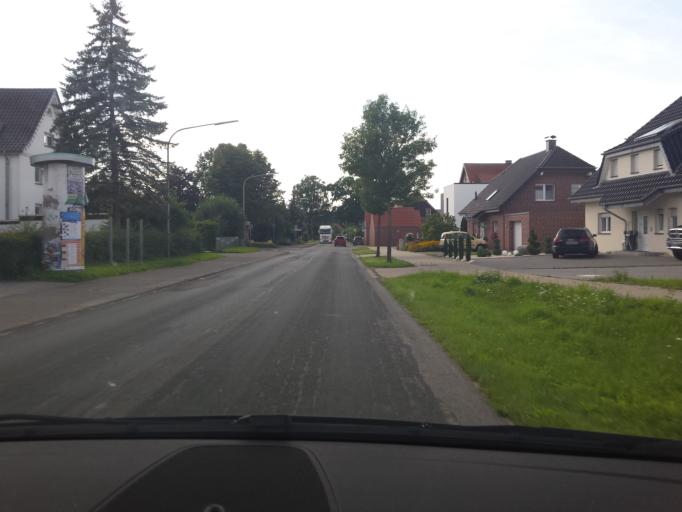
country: DE
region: North Rhine-Westphalia
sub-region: Regierungsbezirk Arnsberg
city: Lippstadt
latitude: 51.6541
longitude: 8.2845
